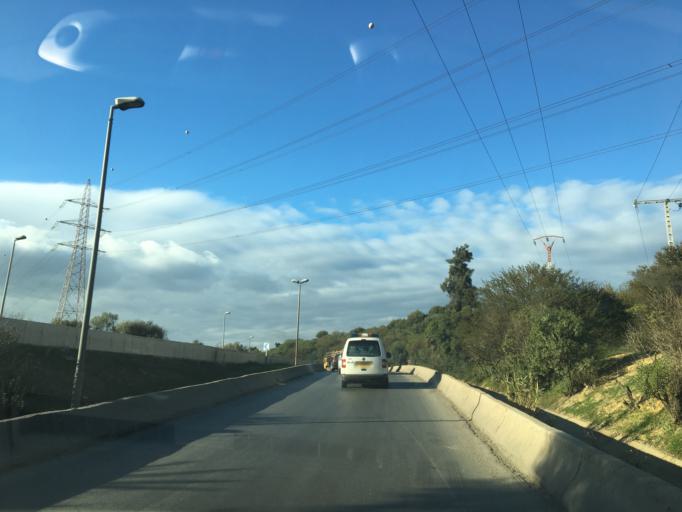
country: DZ
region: Tipaza
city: Baraki
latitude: 36.7101
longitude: 3.1032
